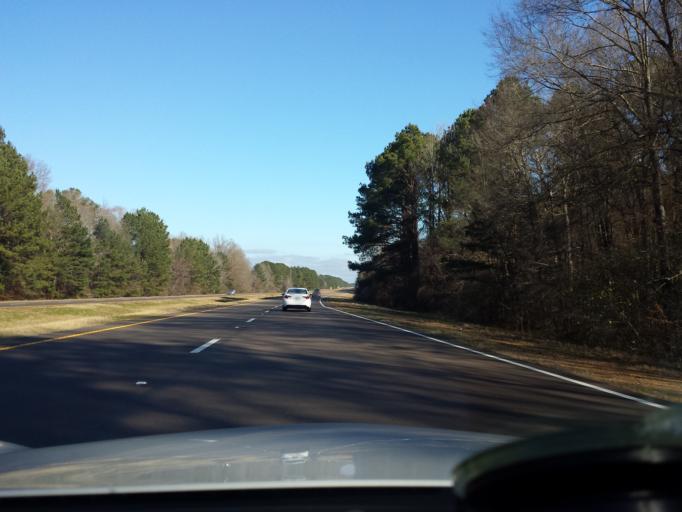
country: US
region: Mississippi
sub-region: Leake County
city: Carthage
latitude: 32.7088
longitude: -89.6264
